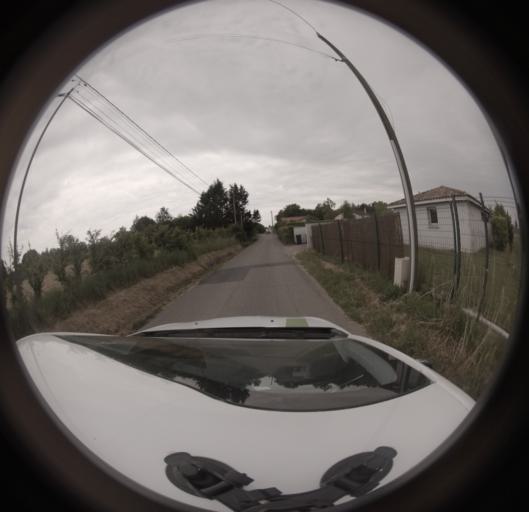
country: FR
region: Midi-Pyrenees
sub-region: Departement du Tarn-et-Garonne
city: Montauban
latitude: 44.0097
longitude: 1.3874
